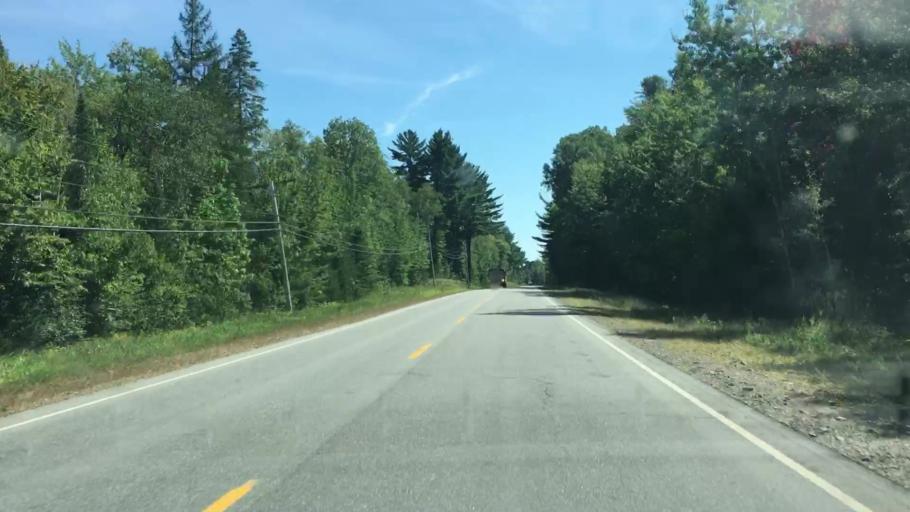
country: US
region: Maine
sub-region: Piscataquis County
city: Milo
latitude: 45.1933
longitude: -68.9003
